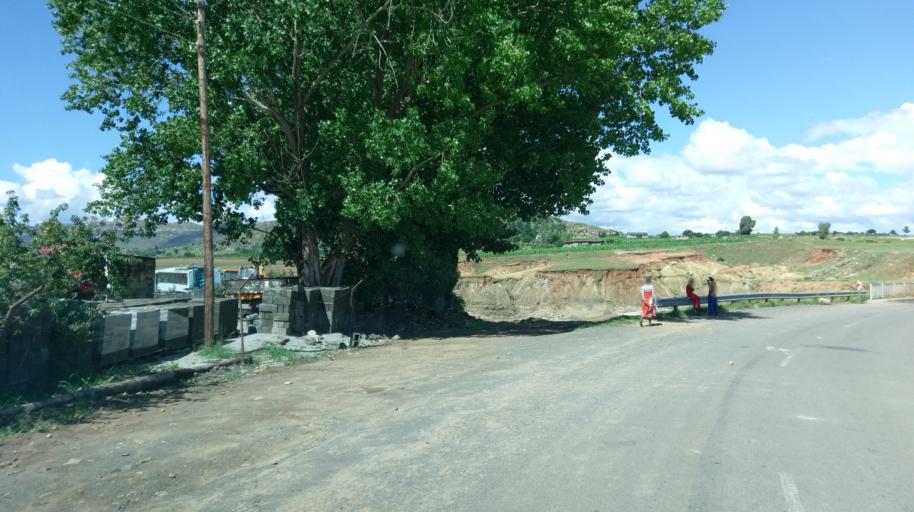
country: LS
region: Mafeteng
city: Mafeteng
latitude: -29.6945
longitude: 27.4447
